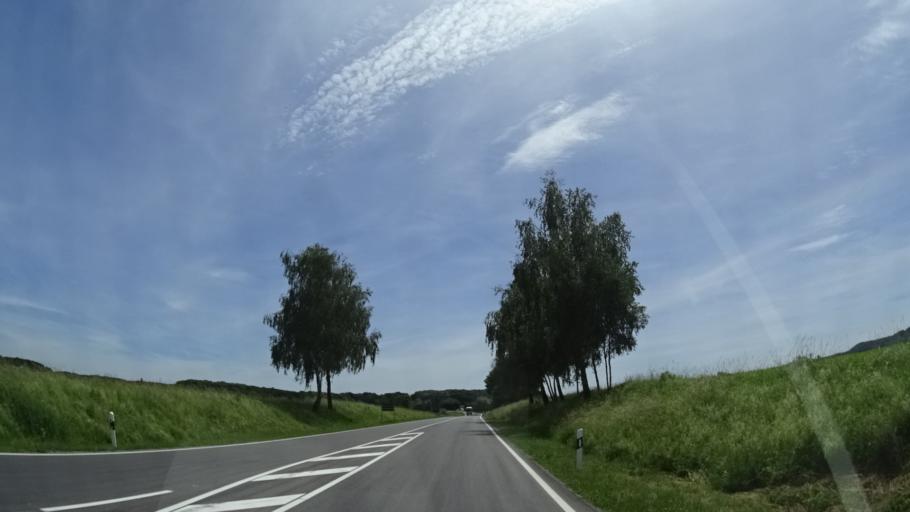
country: DE
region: Baden-Wuerttemberg
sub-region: Regierungsbezirk Stuttgart
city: Kupferzell
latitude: 49.1953
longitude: 9.6910
